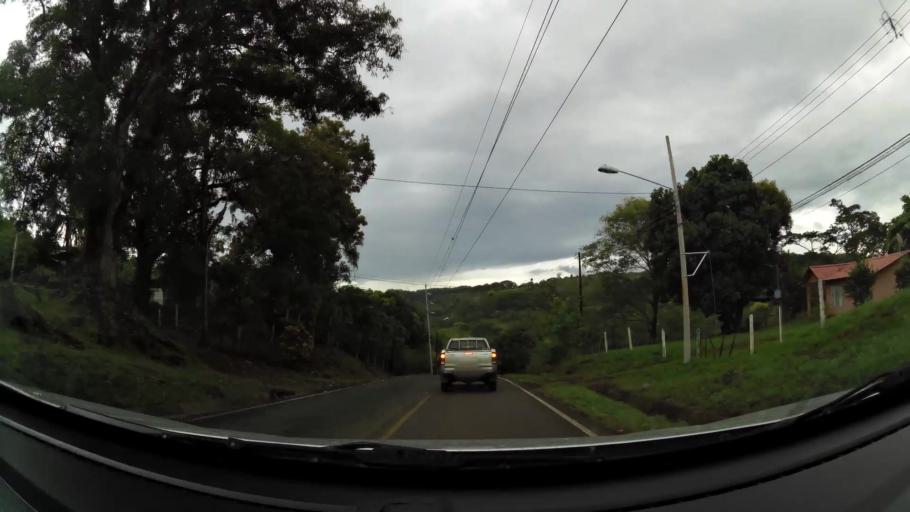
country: CR
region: Alajuela
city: Orotina
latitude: 9.9555
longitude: -84.5700
